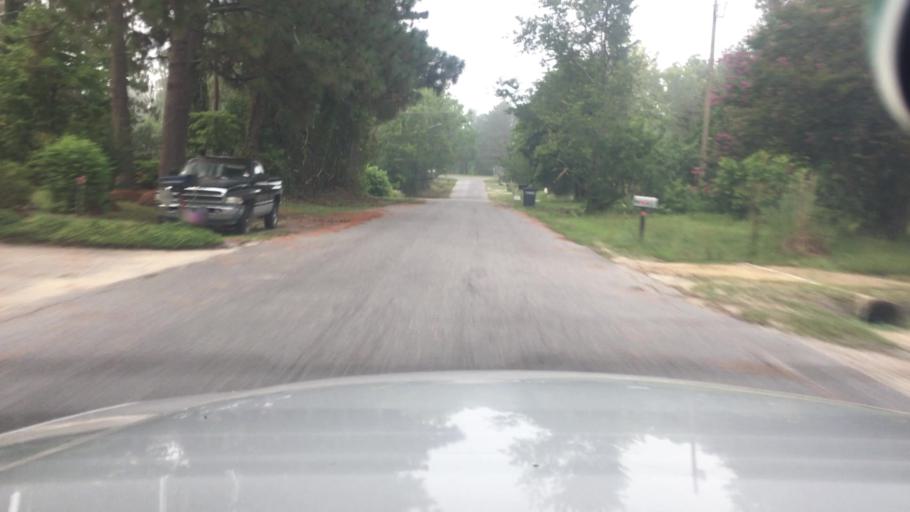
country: US
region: North Carolina
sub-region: Cumberland County
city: Hope Mills
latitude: 35.0184
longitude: -78.9376
